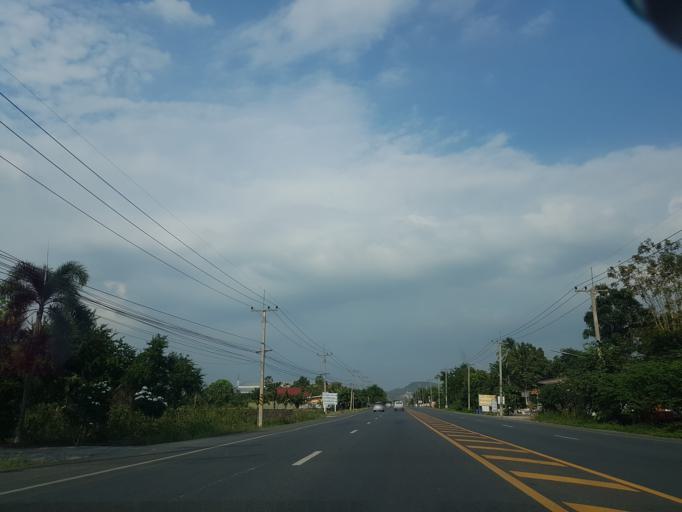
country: TH
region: Sara Buri
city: Ban Mo
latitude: 14.6550
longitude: 100.7638
